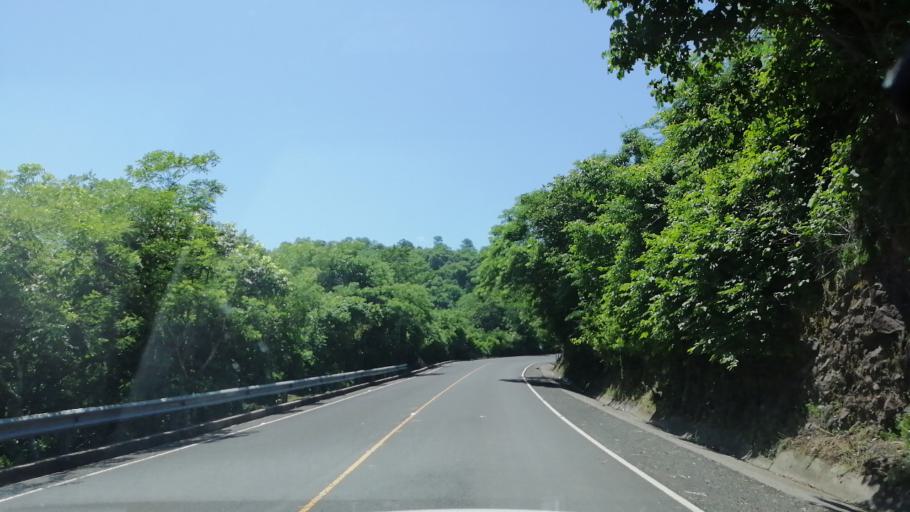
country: SV
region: San Miguel
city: Sesori
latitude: 13.8113
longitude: -88.4041
